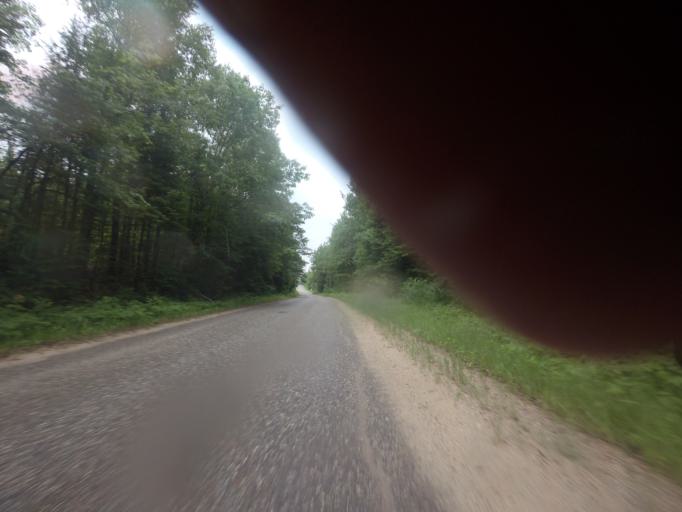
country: CA
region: Quebec
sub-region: Outaouais
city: Maniwaki
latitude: 46.4319
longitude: -75.9473
